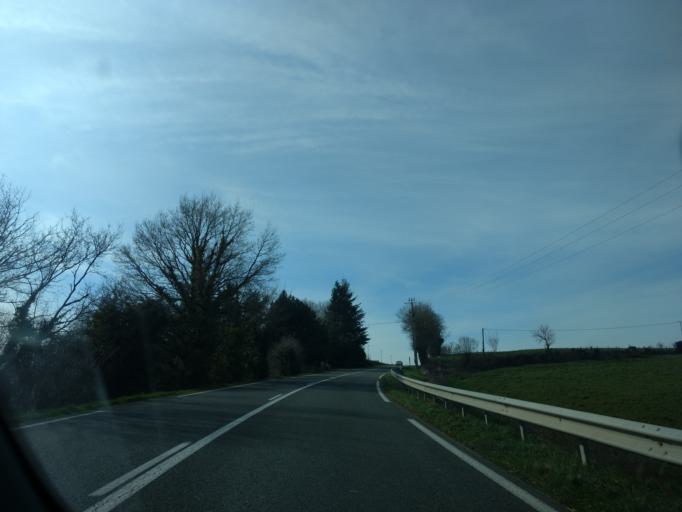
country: FR
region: Midi-Pyrenees
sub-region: Departement de l'Aveyron
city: Villeneuve
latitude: 44.4008
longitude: 2.0863
